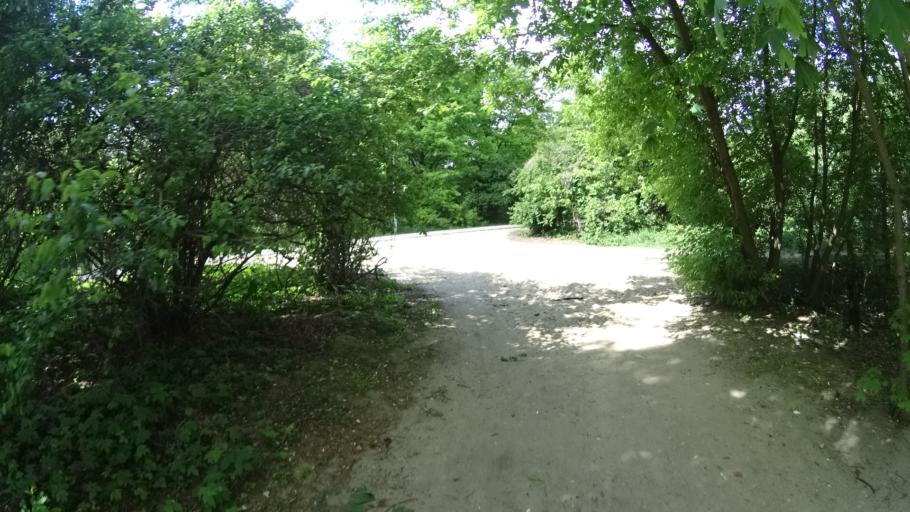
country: PL
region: Masovian Voivodeship
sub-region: Warszawa
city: Bielany
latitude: 52.2804
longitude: 20.9186
